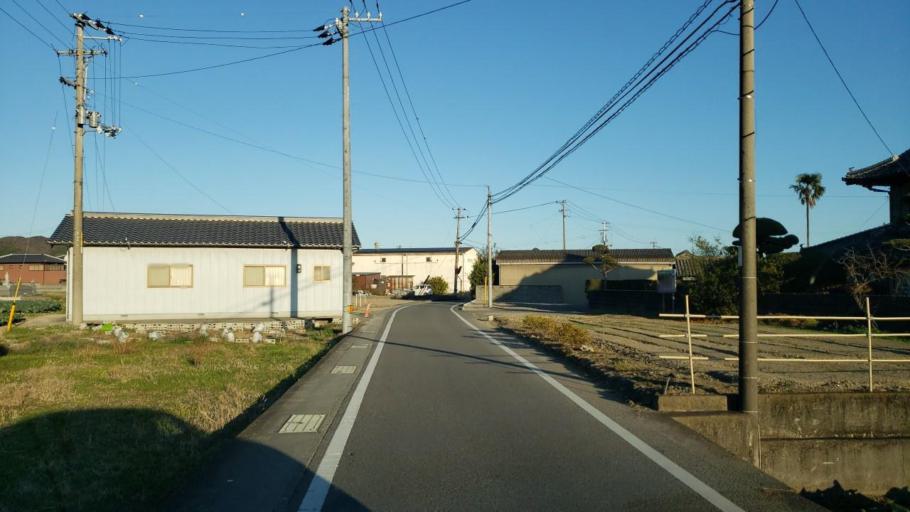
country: JP
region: Tokushima
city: Kamojimacho-jogejima
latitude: 34.0915
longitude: 134.2672
